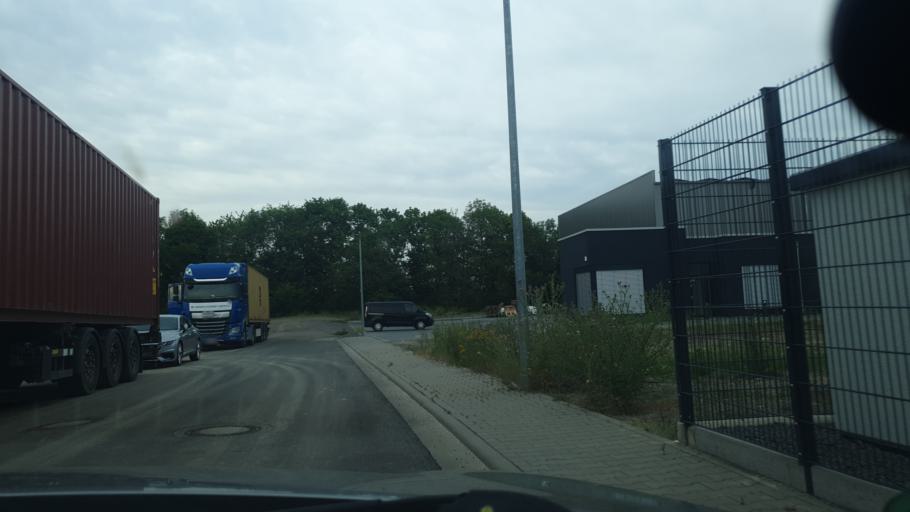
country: DE
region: Rheinland-Pfalz
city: Andernach
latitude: 50.4187
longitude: 7.4178
